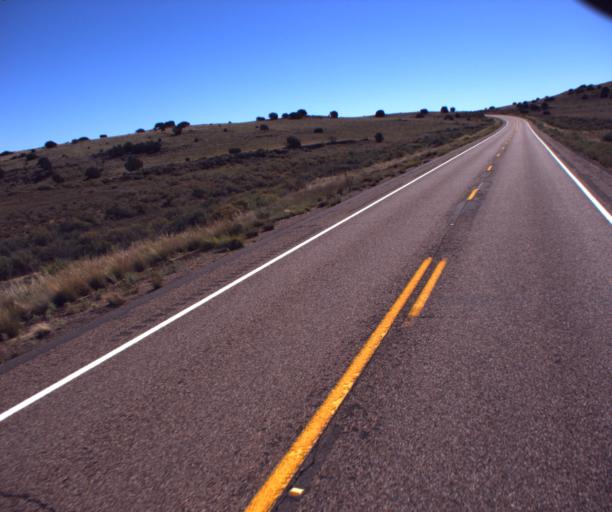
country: US
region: Arizona
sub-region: Apache County
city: Saint Johns
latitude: 34.5645
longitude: -109.5071
